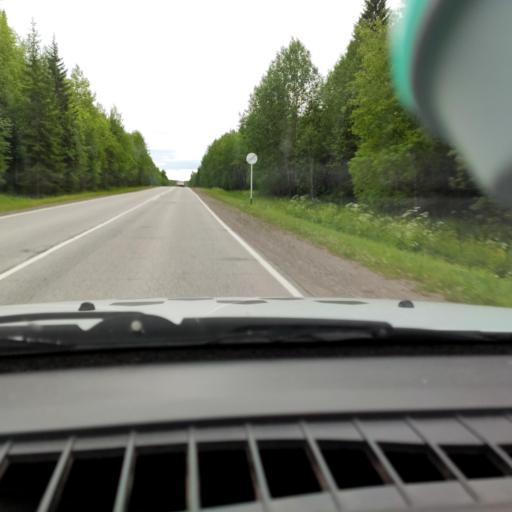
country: RU
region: Perm
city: Lys'va
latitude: 58.1255
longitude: 57.7210
